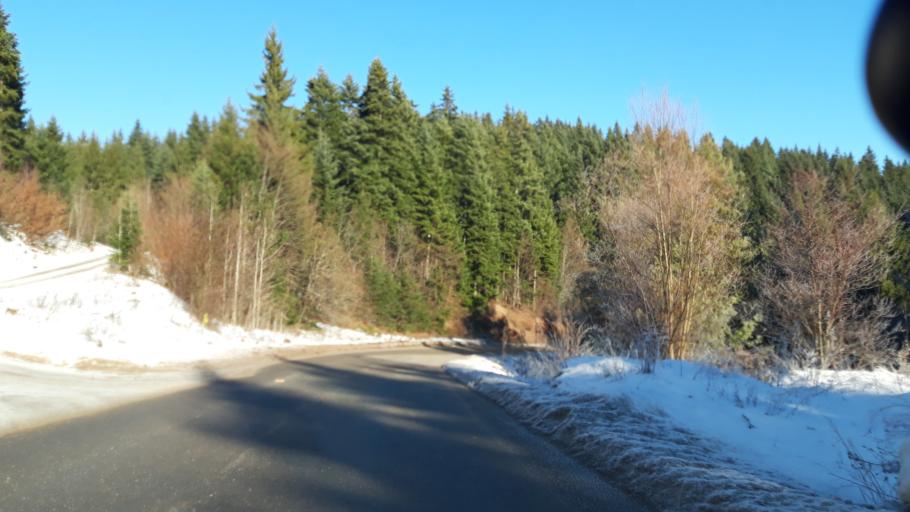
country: BA
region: Republika Srpska
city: Koran
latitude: 43.8024
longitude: 18.5483
